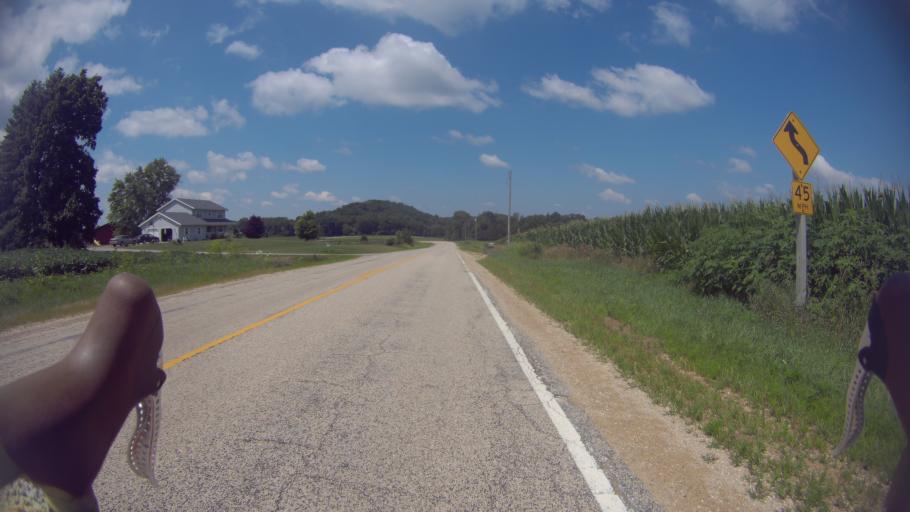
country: US
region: Wisconsin
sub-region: Sauk County
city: Sauk City
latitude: 43.2456
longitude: -89.6286
